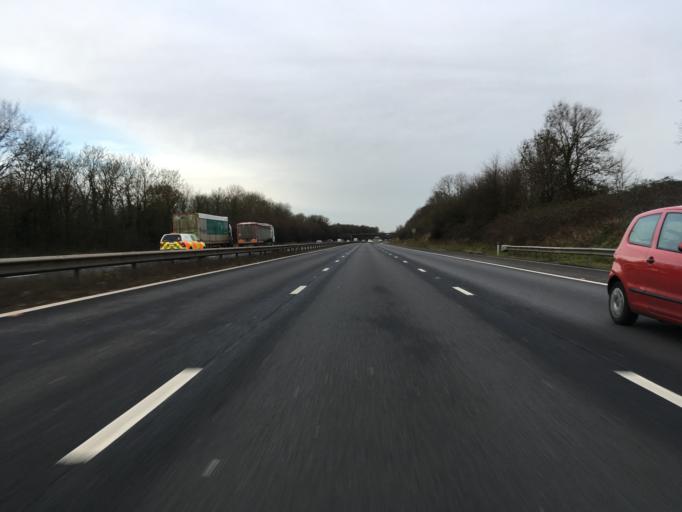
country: GB
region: England
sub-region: Gloucestershire
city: Dursley
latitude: 51.6987
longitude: -2.3920
